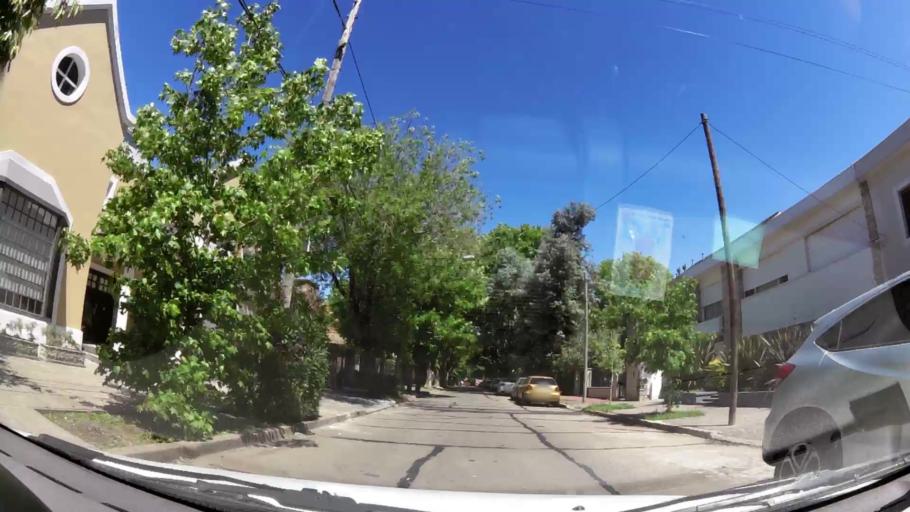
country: AR
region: Buenos Aires
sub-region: Partido de San Isidro
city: San Isidro
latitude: -34.4802
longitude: -58.4914
